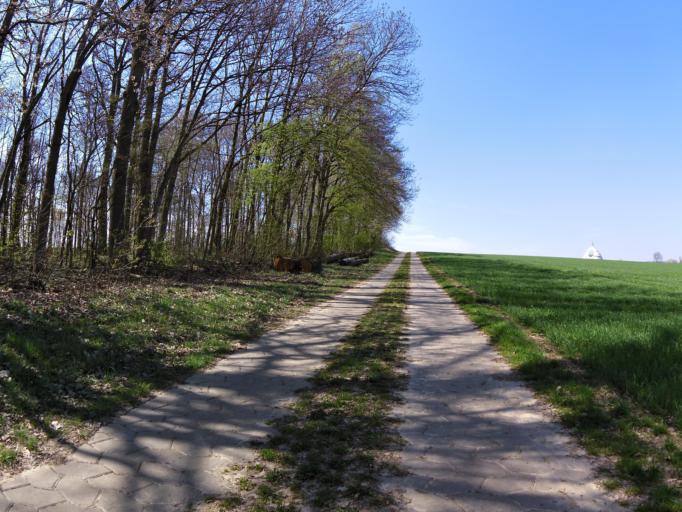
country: DE
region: Bavaria
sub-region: Regierungsbezirk Unterfranken
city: Biebelried
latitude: 49.7767
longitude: 10.0801
